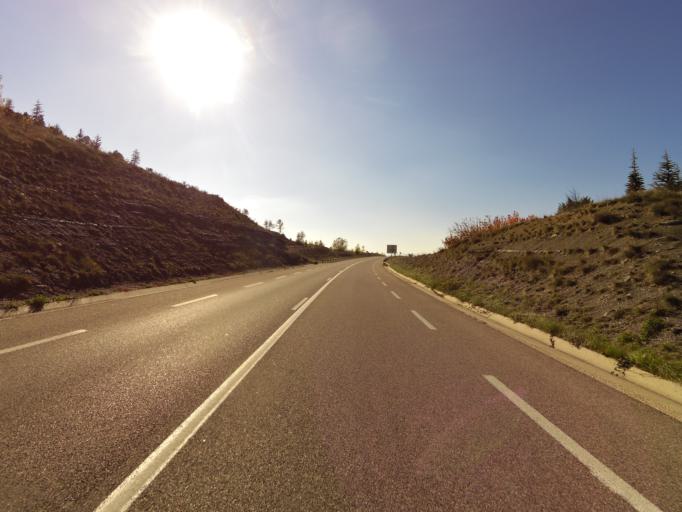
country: FR
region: Rhone-Alpes
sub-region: Departement de l'Ardeche
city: Lachapelle-sous-Aubenas
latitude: 44.5427
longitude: 4.3543
